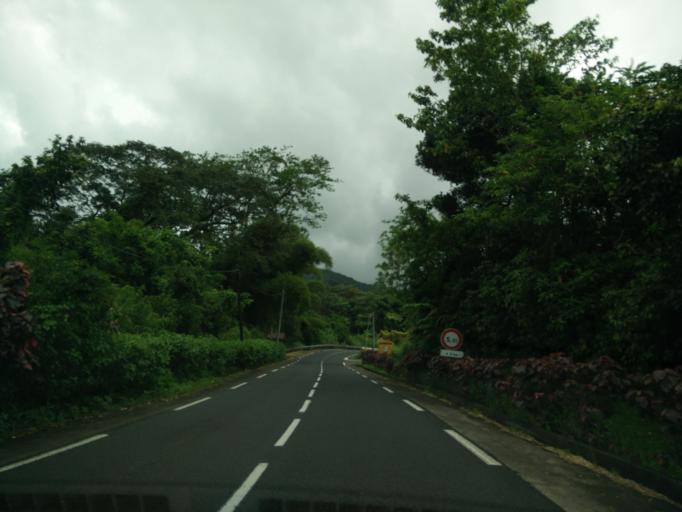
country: MQ
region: Martinique
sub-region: Martinique
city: Le Morne-Rouge
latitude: 14.7547
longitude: -61.1083
